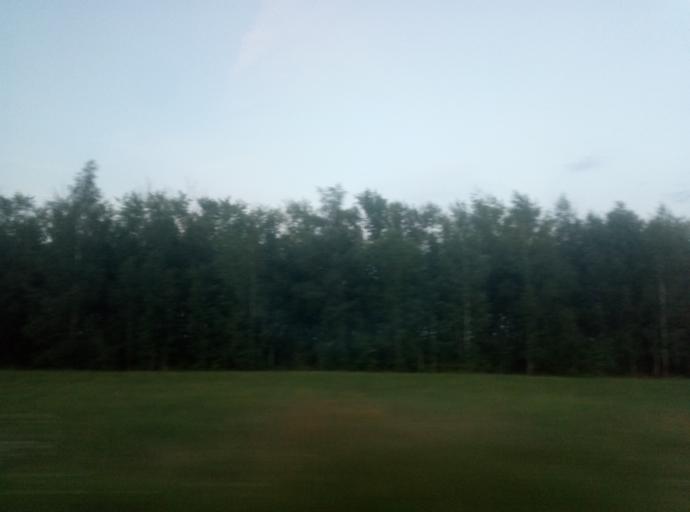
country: RU
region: Tula
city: Kireyevsk
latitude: 53.8547
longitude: 37.8787
